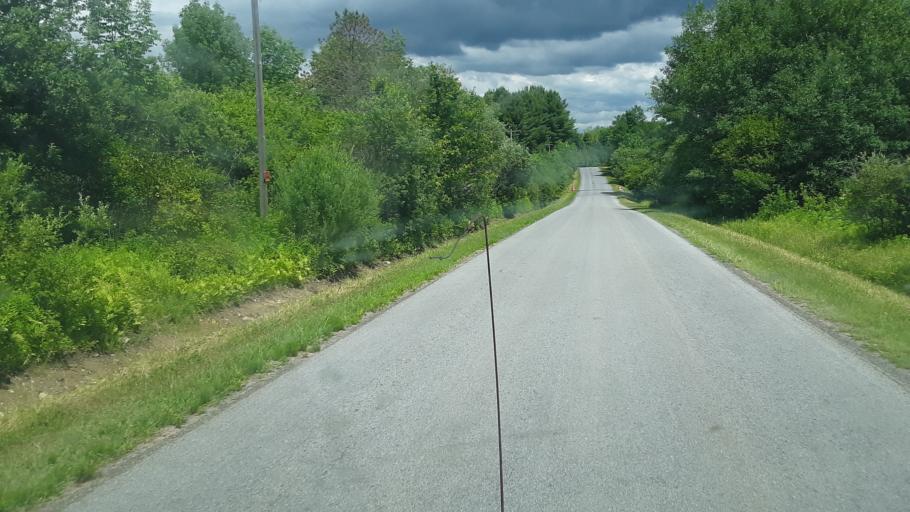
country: US
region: New York
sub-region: Oneida County
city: Rome
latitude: 43.3935
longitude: -75.5087
